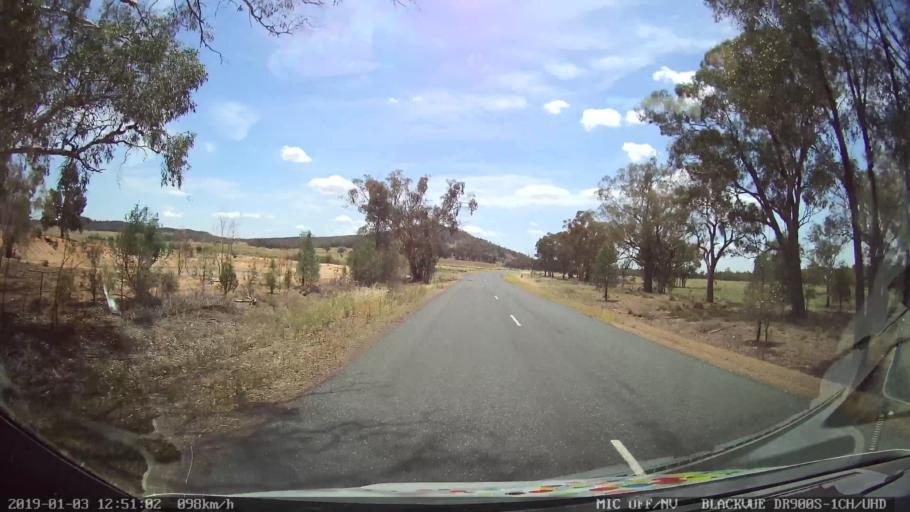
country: AU
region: New South Wales
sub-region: Weddin
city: Grenfell
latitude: -33.6841
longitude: 148.2760
